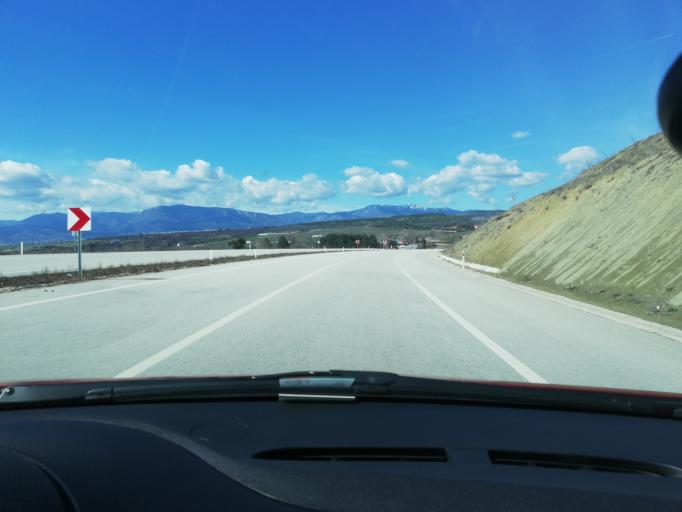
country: TR
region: Karabuk
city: Safranbolu
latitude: 41.2166
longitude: 32.7874
